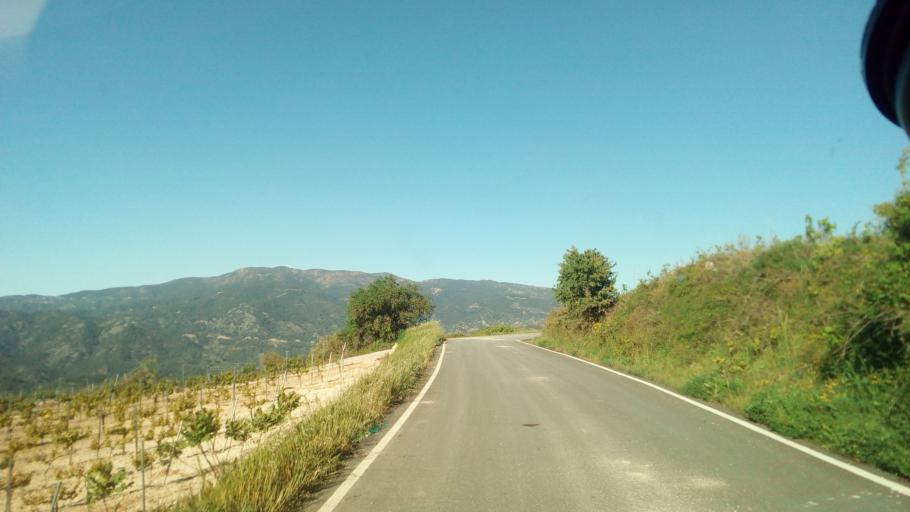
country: CY
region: Limassol
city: Pachna
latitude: 34.8661
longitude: 32.7753
